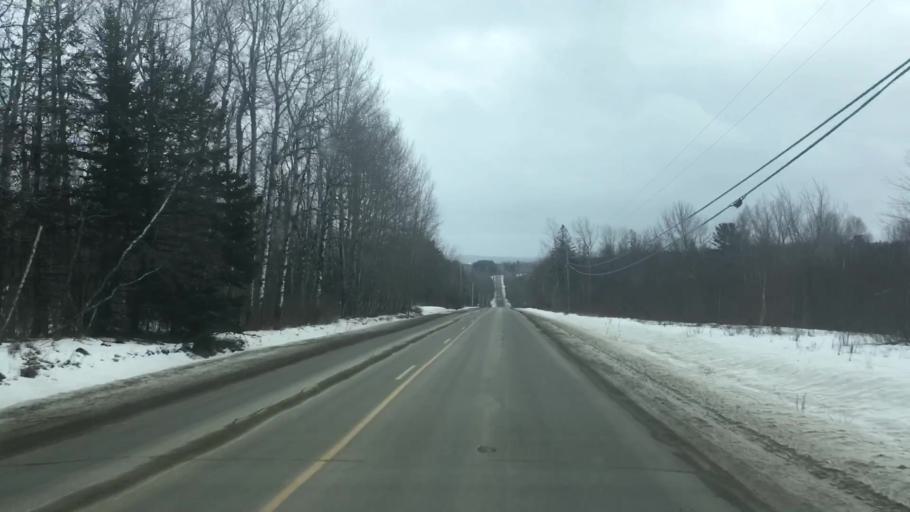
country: US
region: Maine
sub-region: Washington County
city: East Machias
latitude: 44.9728
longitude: -67.4491
